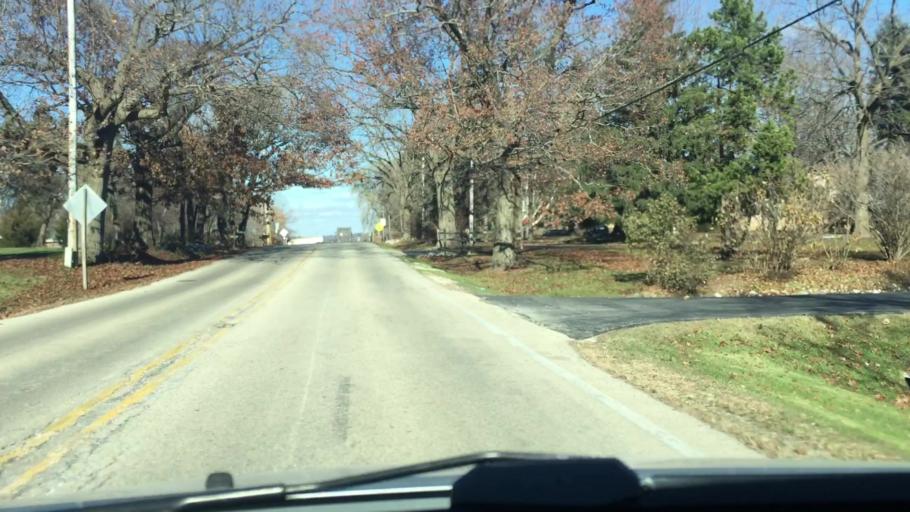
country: US
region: Wisconsin
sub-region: Waukesha County
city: Pewaukee
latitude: 43.0550
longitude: -88.3042
